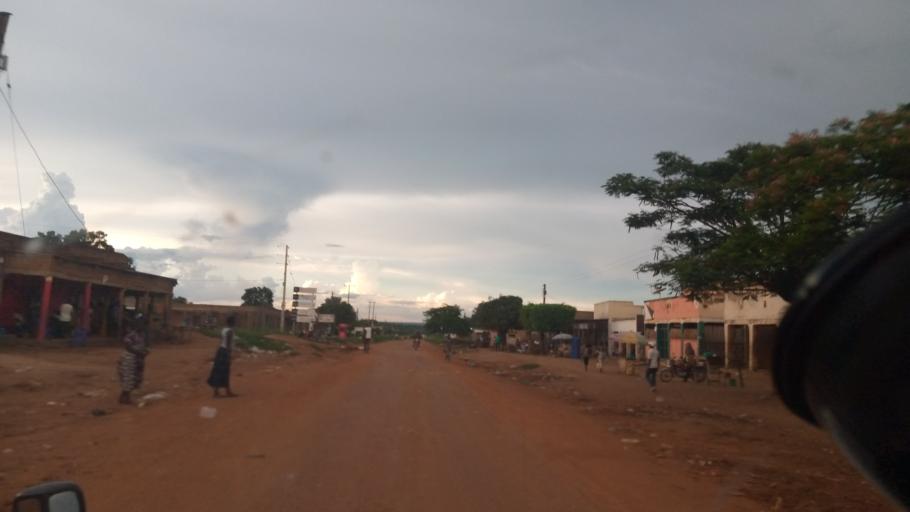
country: UG
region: Northern Region
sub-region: Kole District
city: Kole
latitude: 2.4875
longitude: 32.9351
